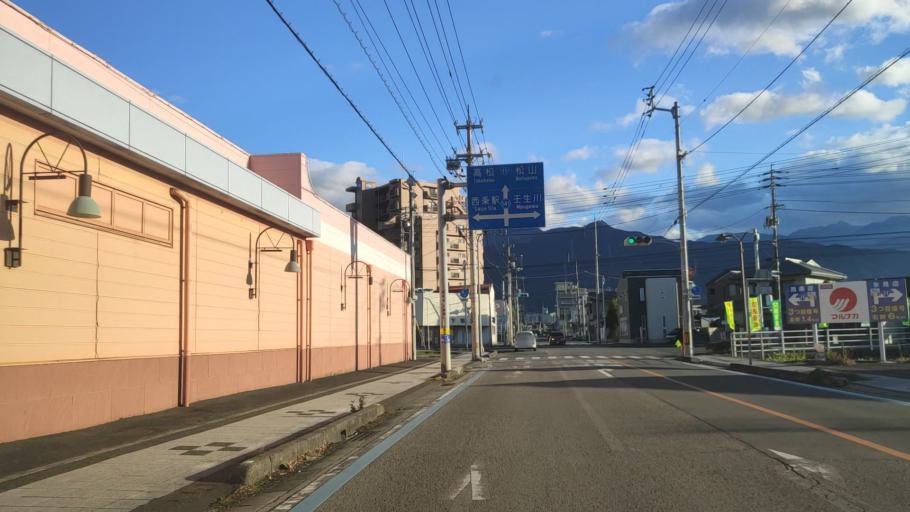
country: JP
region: Ehime
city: Saijo
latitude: 33.9120
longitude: 133.1799
